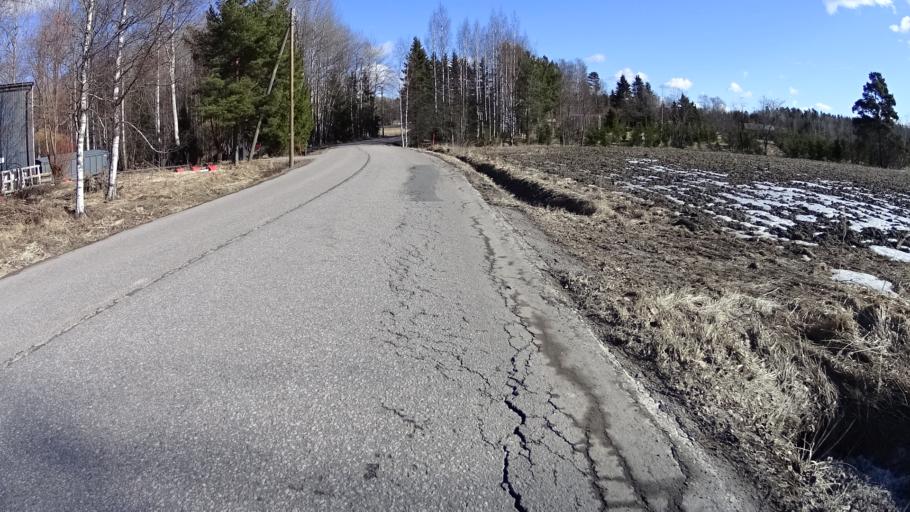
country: FI
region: Uusimaa
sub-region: Helsinki
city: Kauniainen
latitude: 60.2731
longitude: 24.7114
